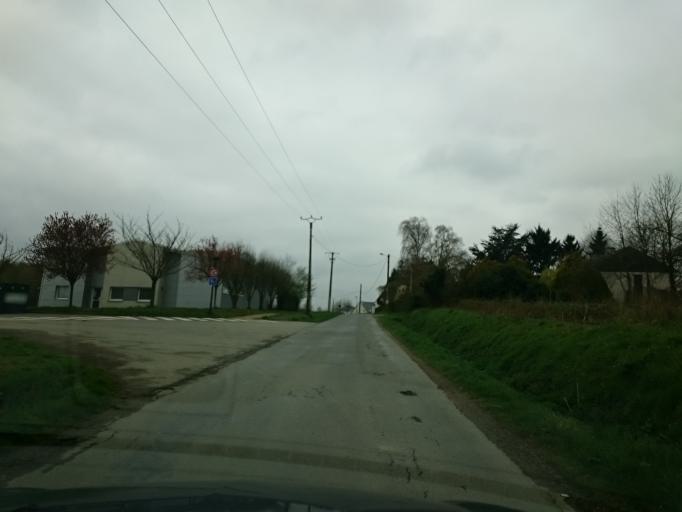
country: FR
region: Brittany
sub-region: Departement d'Ille-et-Vilaine
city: Corps-Nuds
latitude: 47.9859
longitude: -1.5783
